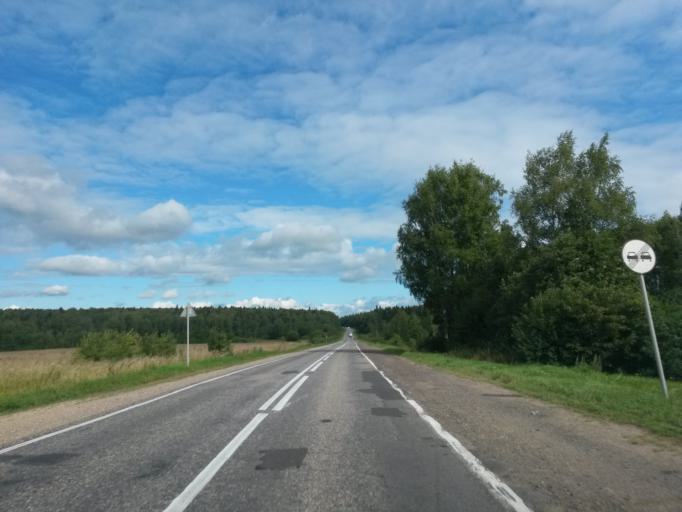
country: RU
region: Jaroslavl
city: Krasnyye Tkachi
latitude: 57.4627
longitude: 39.9085
